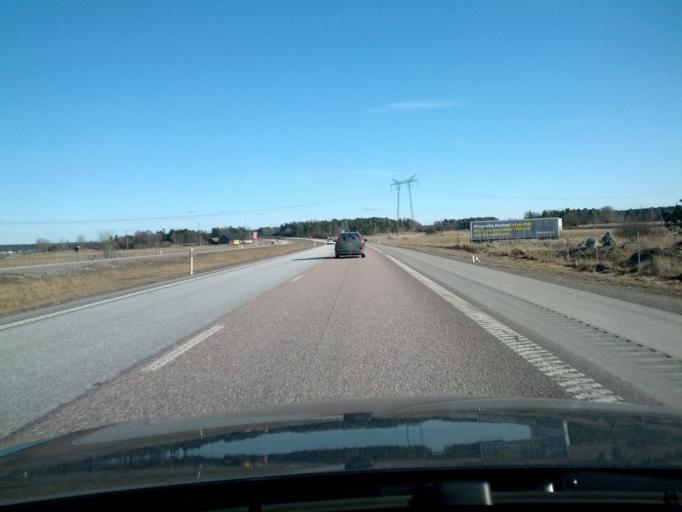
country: SE
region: Uppsala
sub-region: Habo Kommun
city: Balsta
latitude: 59.5971
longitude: 17.4503
